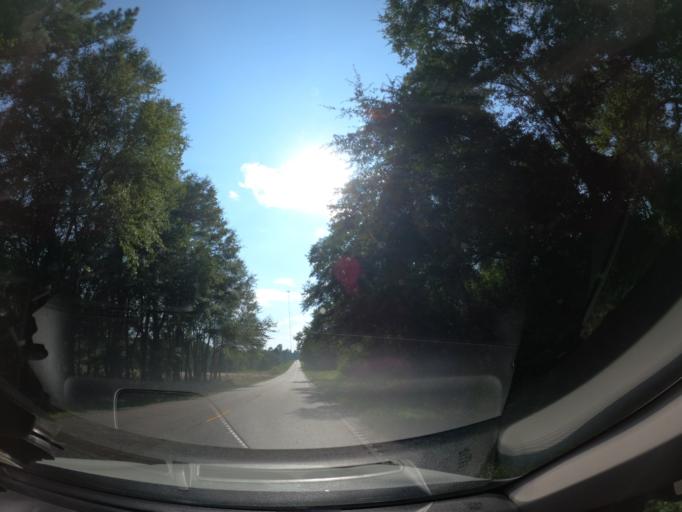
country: US
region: South Carolina
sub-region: Aiken County
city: Jackson
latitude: 33.4094
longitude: -81.8161
